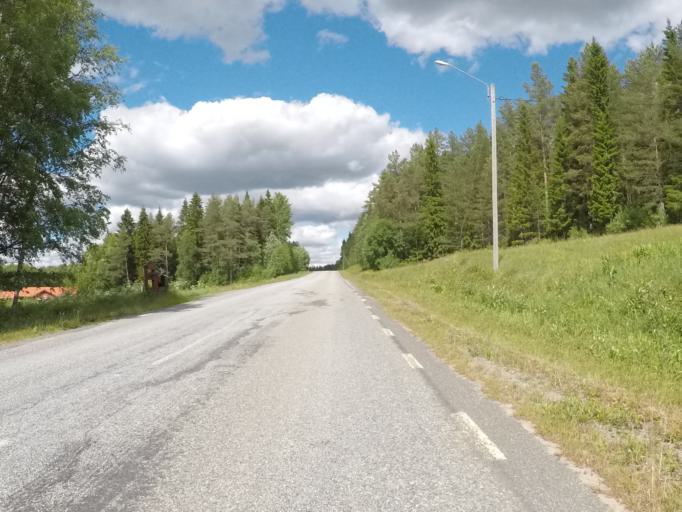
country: SE
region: Vaesterbotten
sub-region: Robertsfors Kommun
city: Robertsfors
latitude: 63.9883
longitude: 20.8115
